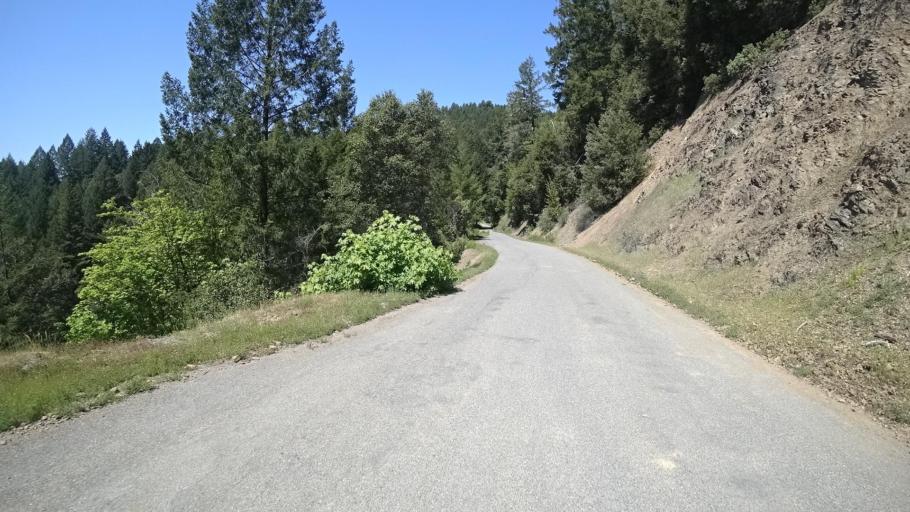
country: US
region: California
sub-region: Humboldt County
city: Redway
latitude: 40.1955
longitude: -123.5550
